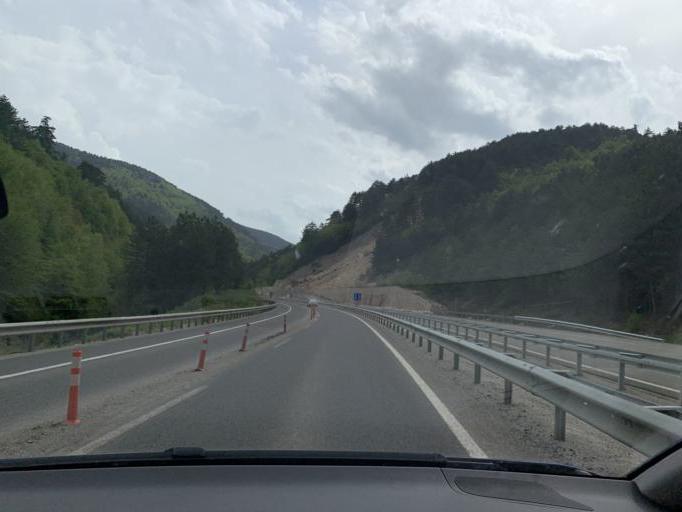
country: TR
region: Bolu
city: Mengen
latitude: 40.8603
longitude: 32.0770
